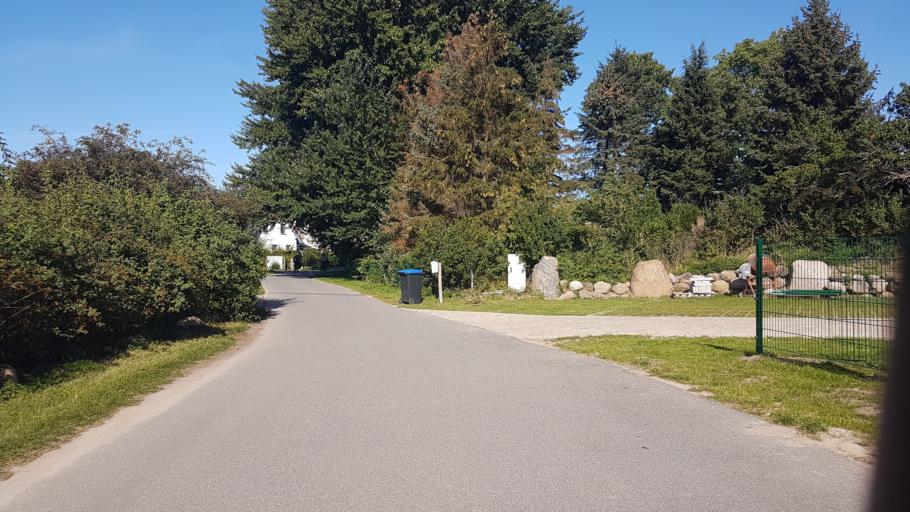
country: DE
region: Mecklenburg-Vorpommern
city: Glowe
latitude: 54.5655
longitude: 13.4753
